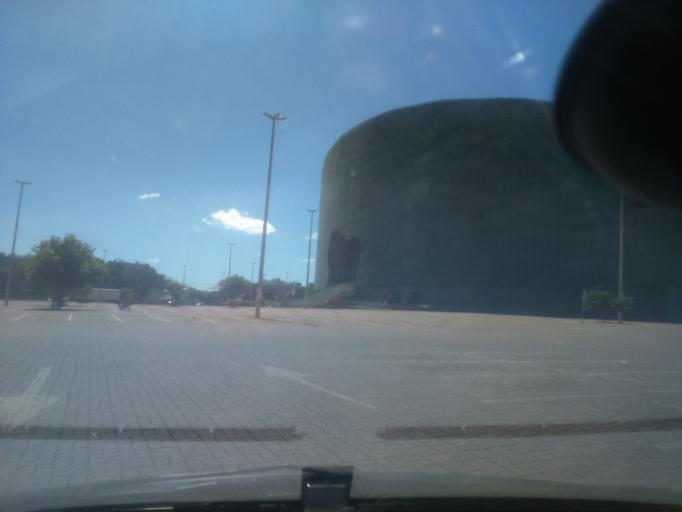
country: BR
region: Goias
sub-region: Luziania
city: Luziania
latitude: -16.0122
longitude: -48.0631
